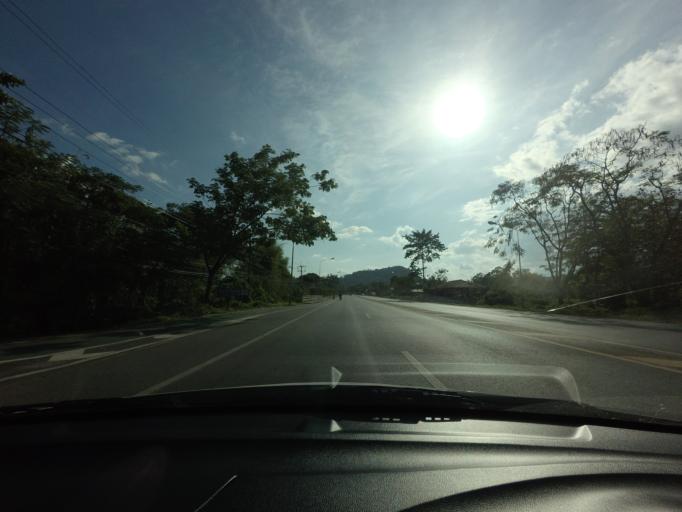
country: TH
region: Nakhon Nayok
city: Nakhon Nayok
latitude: 14.3118
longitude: 101.2957
